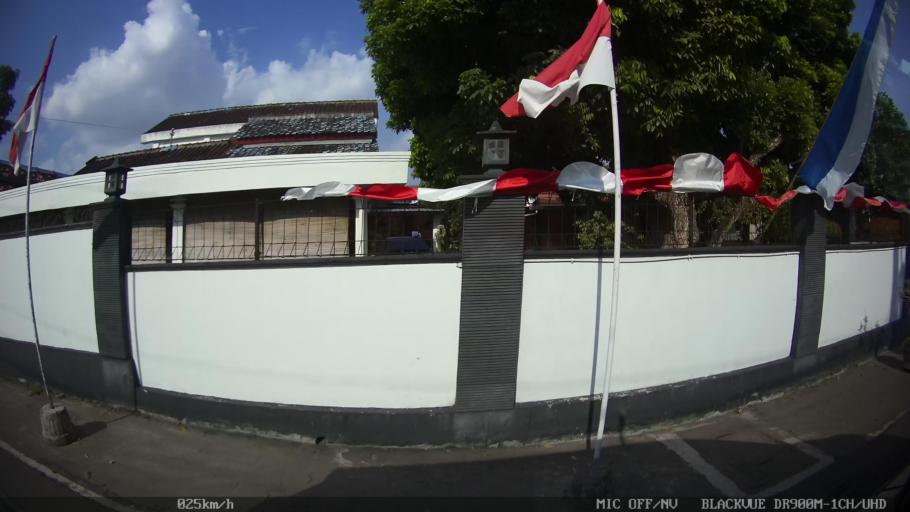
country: ID
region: Daerah Istimewa Yogyakarta
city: Yogyakarta
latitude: -7.8217
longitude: 110.3788
